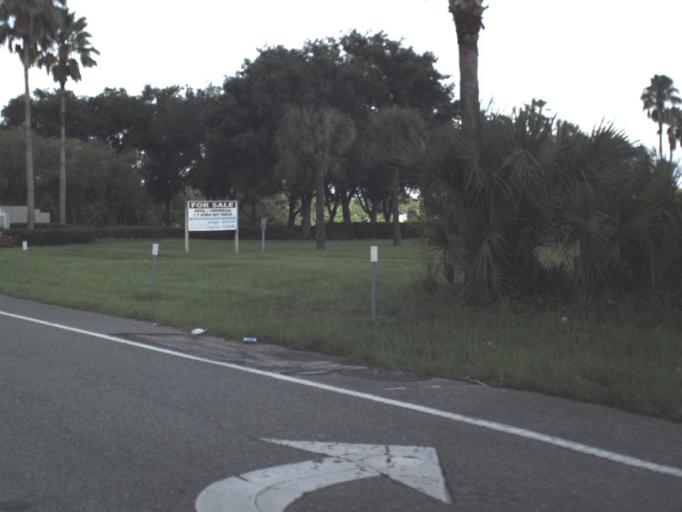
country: US
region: Florida
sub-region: Hillsborough County
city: East Lake-Orient Park
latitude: 27.9816
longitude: -82.3869
